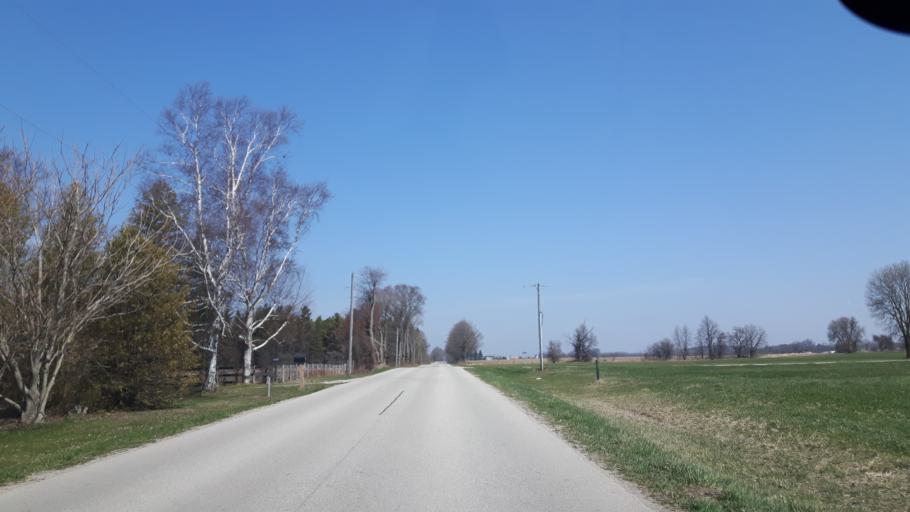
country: CA
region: Ontario
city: Goderich
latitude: 43.6294
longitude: -81.6846
